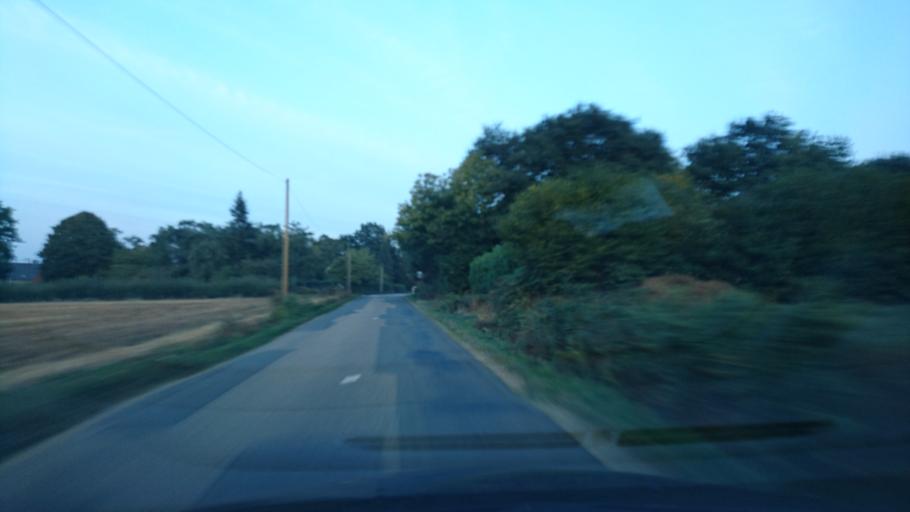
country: FR
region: Brittany
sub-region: Departement d'Ille-et-Vilaine
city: Guignen
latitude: 47.9132
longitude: -1.8813
